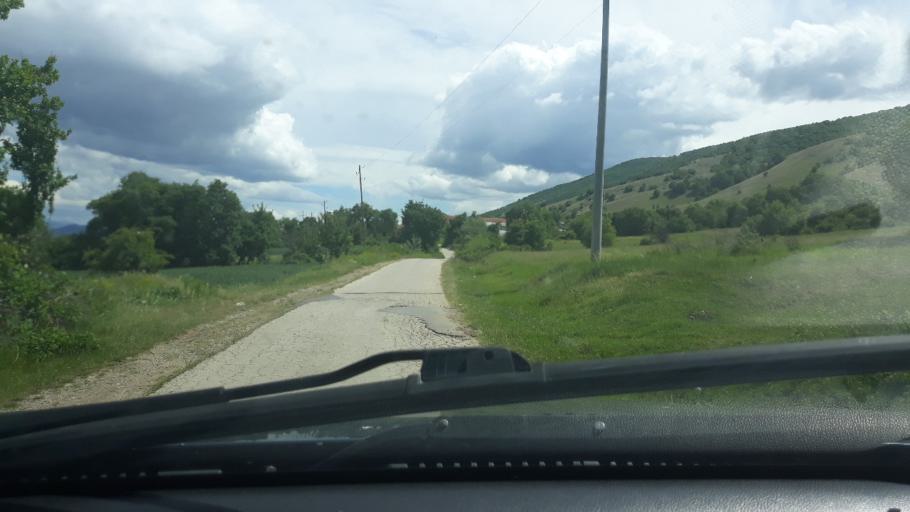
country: MK
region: Krivogastani
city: Krivogashtani
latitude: 41.3265
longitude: 21.3035
